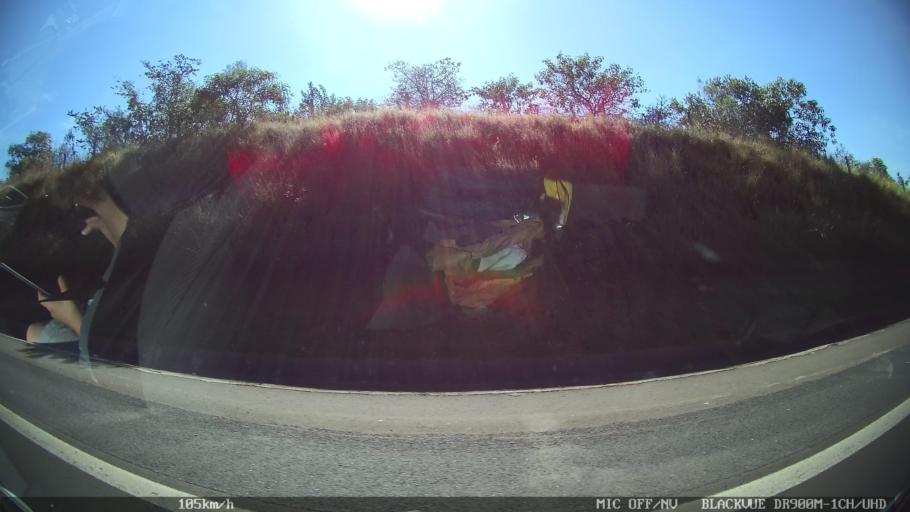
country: BR
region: Sao Paulo
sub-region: Franca
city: Franca
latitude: -20.5544
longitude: -47.4259
